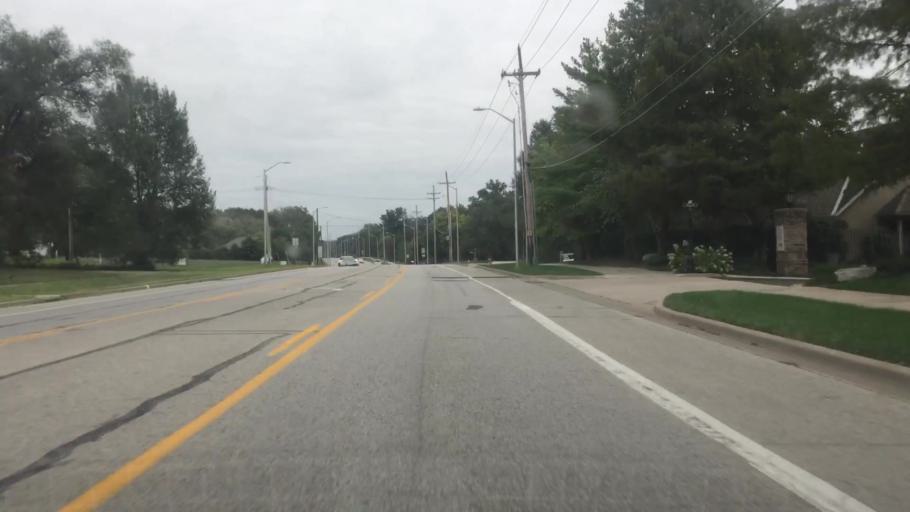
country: US
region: Kansas
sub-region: Johnson County
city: Lenexa
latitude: 38.9986
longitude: -94.7723
